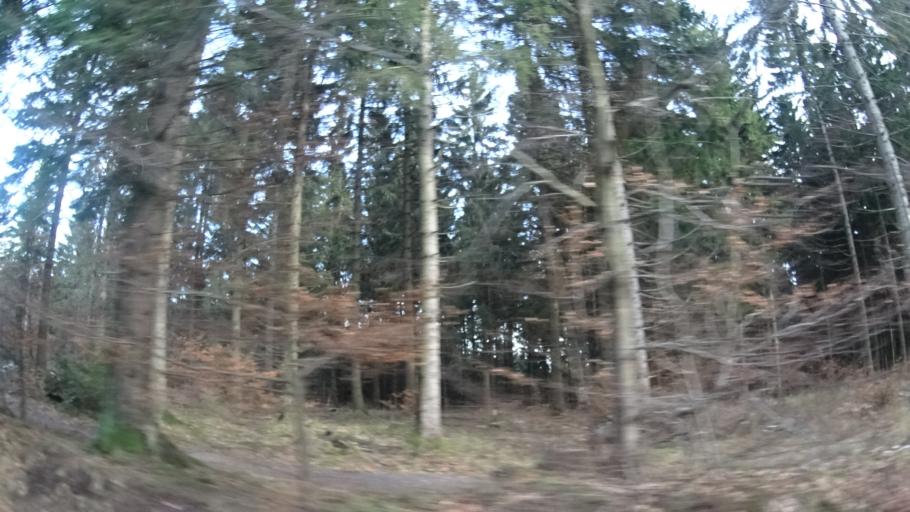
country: DE
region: Thuringia
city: Tabarz
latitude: 50.8334
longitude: 10.5254
